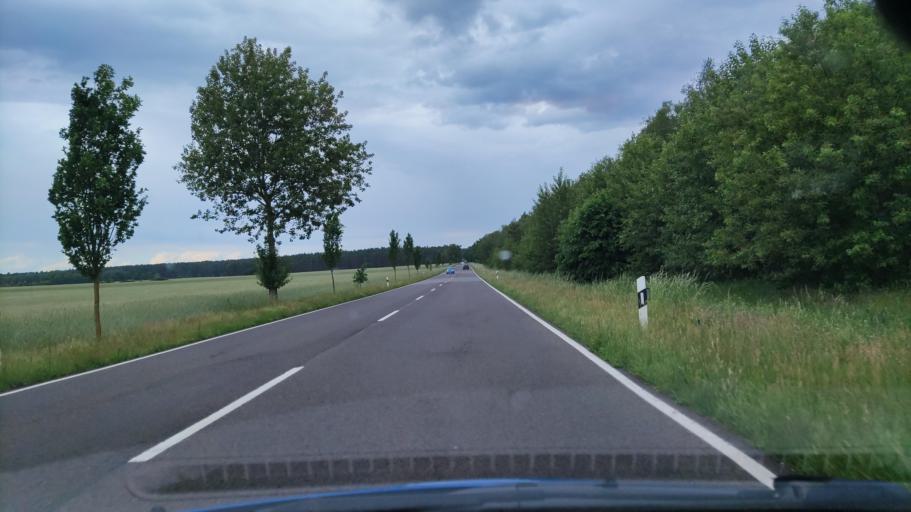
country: DE
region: Saxony-Anhalt
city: Letzlingen
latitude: 52.4107
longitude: 11.4779
